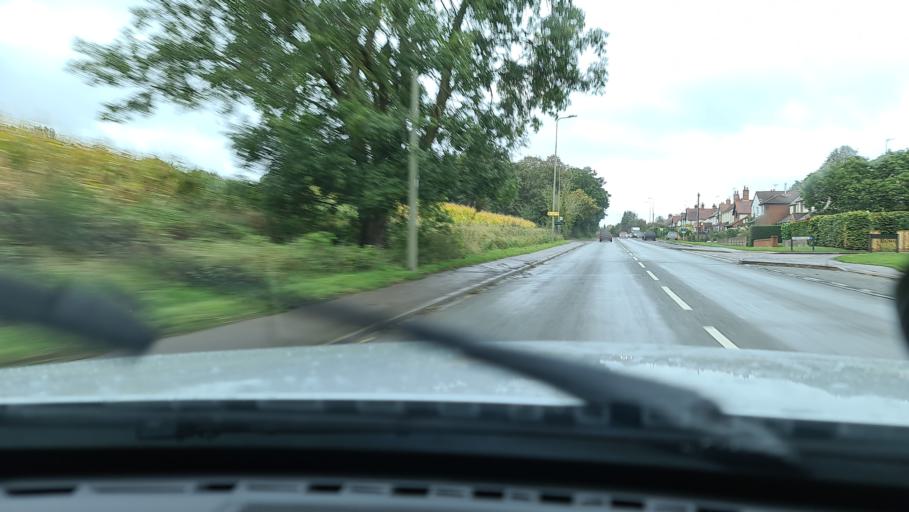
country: GB
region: England
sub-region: Oxfordshire
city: Adderbury
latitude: 52.0223
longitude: -1.3117
